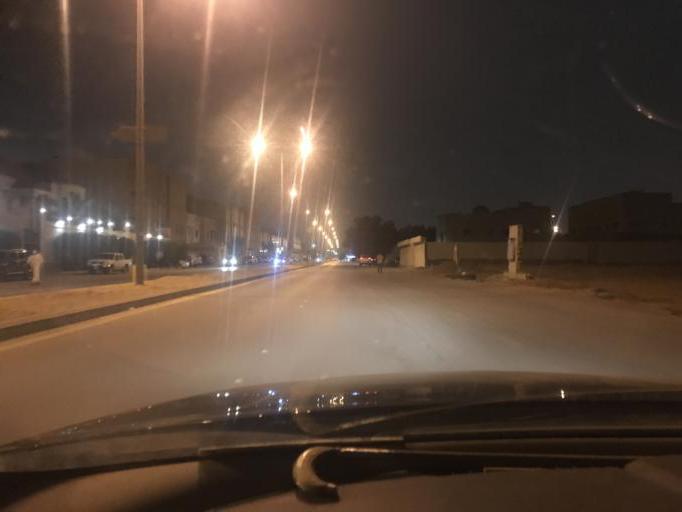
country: SA
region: Ar Riyad
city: Riyadh
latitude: 24.7528
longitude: 46.7767
